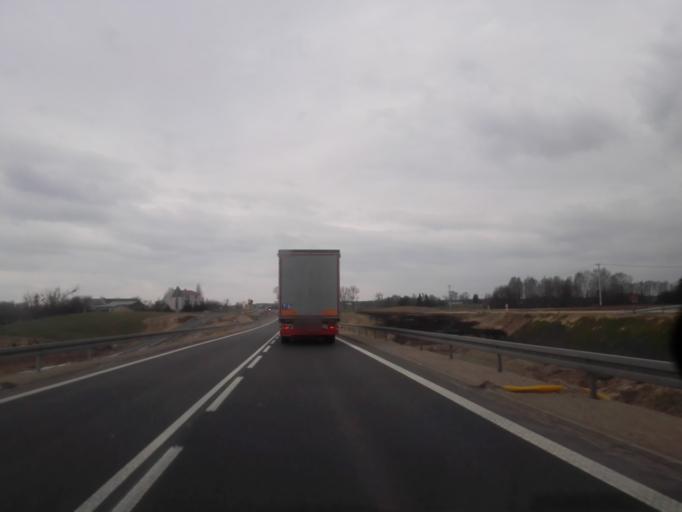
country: PL
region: Podlasie
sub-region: Powiat augustowski
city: Augustow
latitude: 53.7847
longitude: 22.8493
